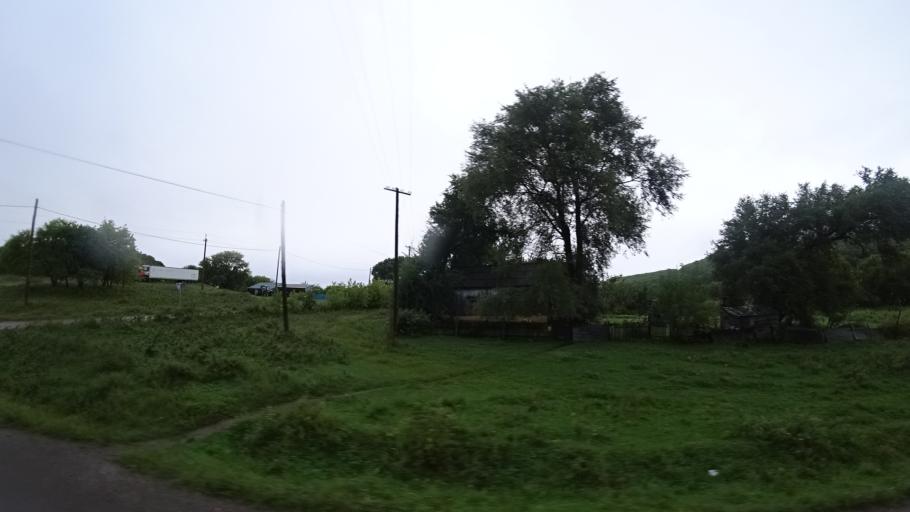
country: RU
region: Primorskiy
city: Monastyrishche
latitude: 44.2574
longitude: 132.4192
